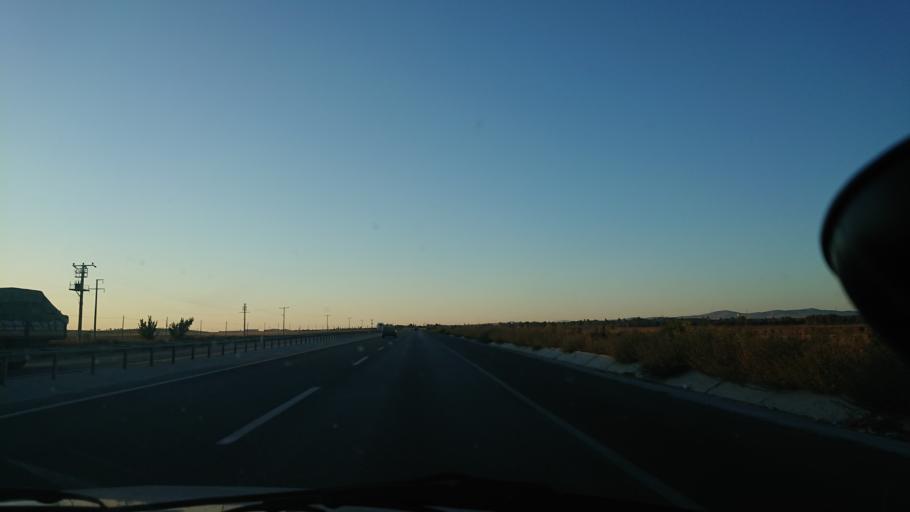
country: TR
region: Eskisehir
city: Mahmudiye
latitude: 39.5504
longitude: 30.9273
